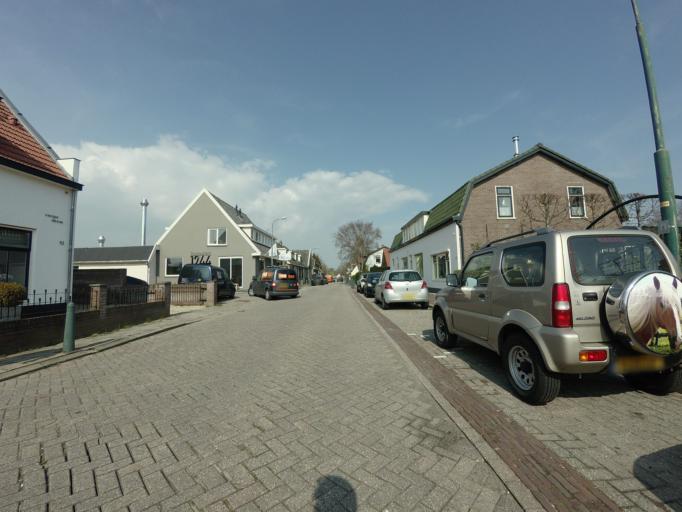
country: NL
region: North Holland
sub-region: Gemeente Wijdemeren
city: Kortenhoef
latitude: 52.2632
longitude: 5.0971
